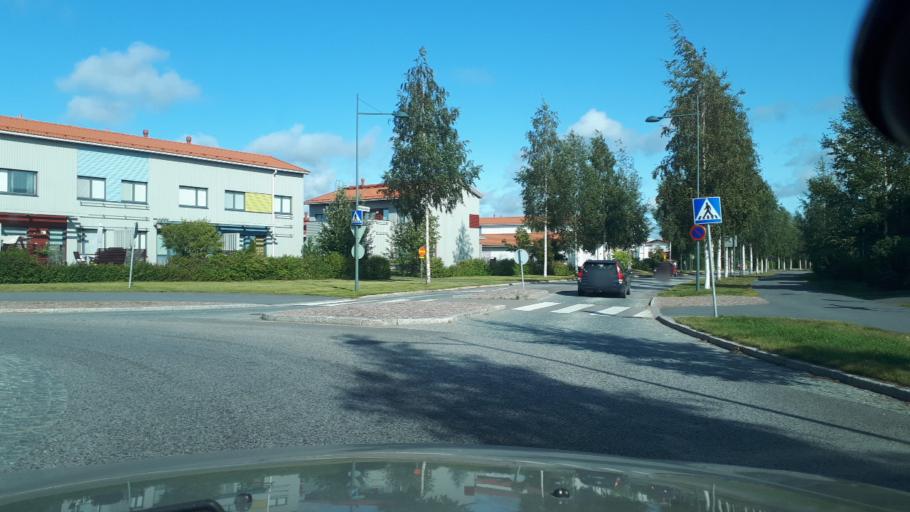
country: FI
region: Northern Ostrobothnia
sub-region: Oulu
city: Oulu
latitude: 65.0719
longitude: 25.4481
